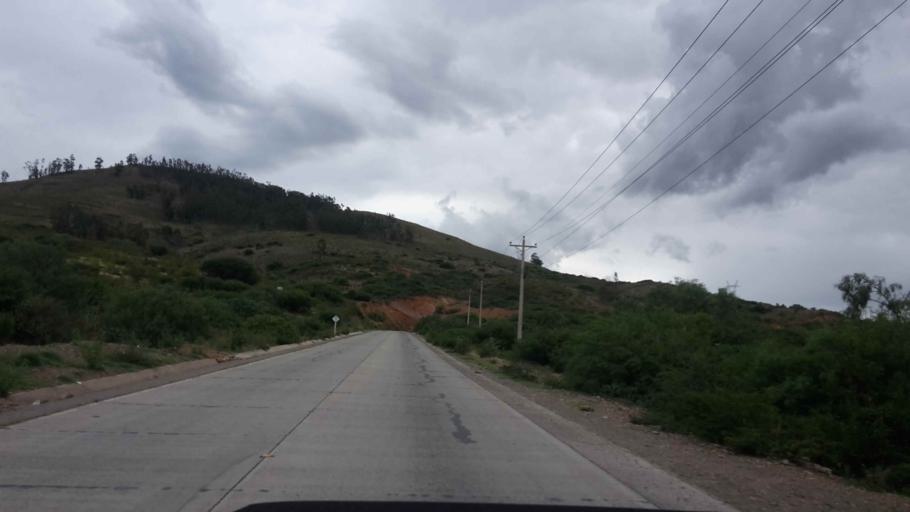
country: BO
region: Cochabamba
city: Cochabamba
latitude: -17.5338
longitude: -66.2026
